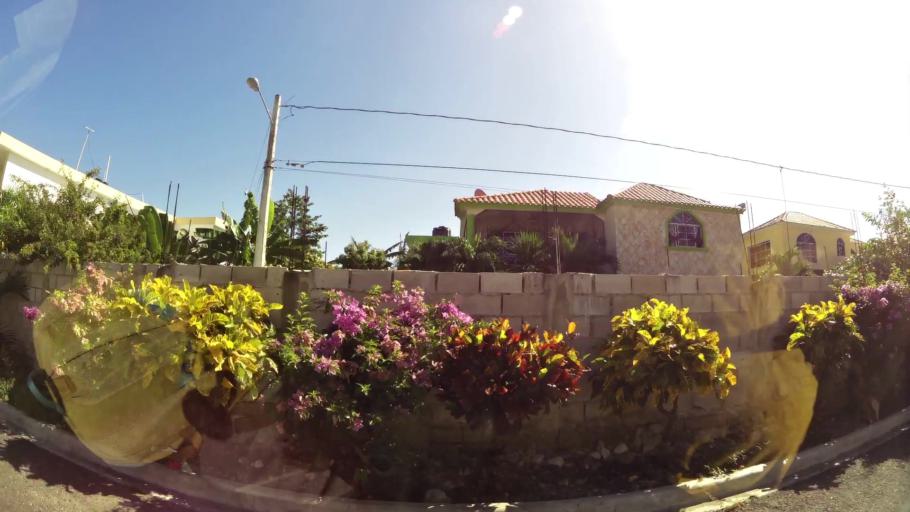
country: DO
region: San Cristobal
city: San Cristobal
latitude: 18.4306
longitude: -70.1234
